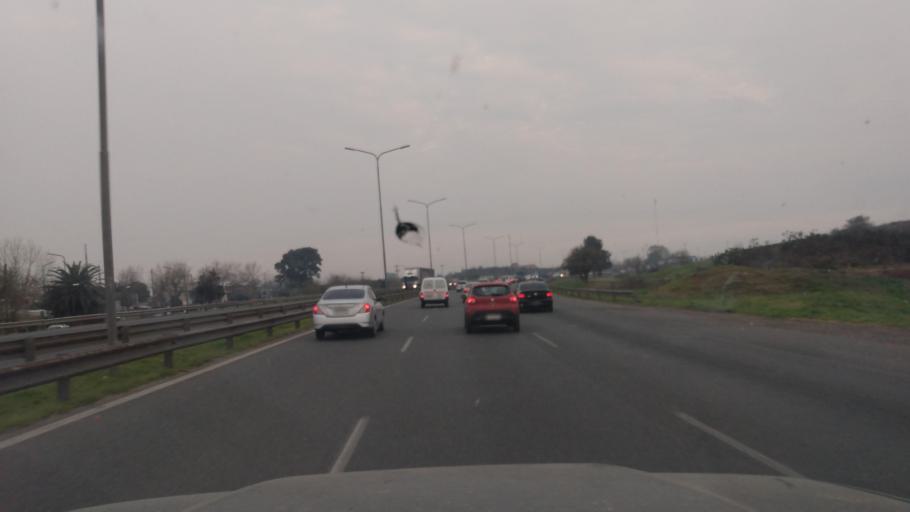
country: AR
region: Buenos Aires
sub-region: Partido de Tigre
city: Tigre
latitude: -34.4982
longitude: -58.5911
